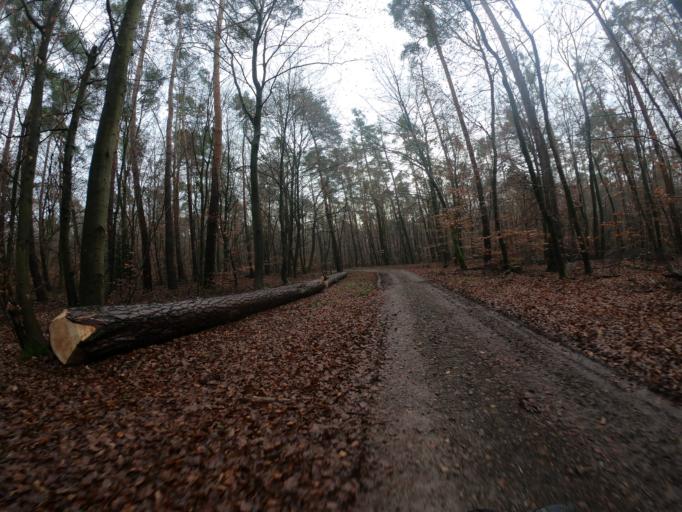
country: DE
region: Hesse
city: Morfelden-Walldorf
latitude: 49.9816
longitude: 8.6101
